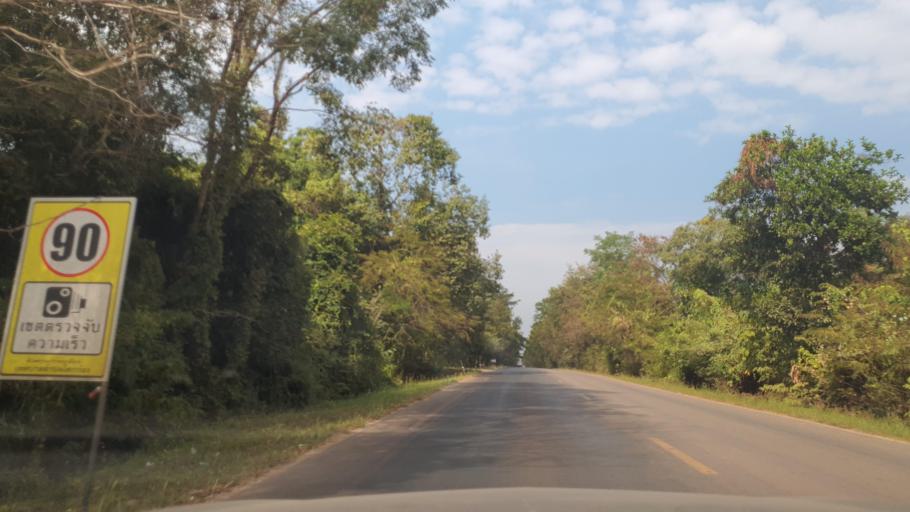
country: TH
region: Changwat Bueng Kan
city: Si Wilai
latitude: 18.2848
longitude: 103.8263
